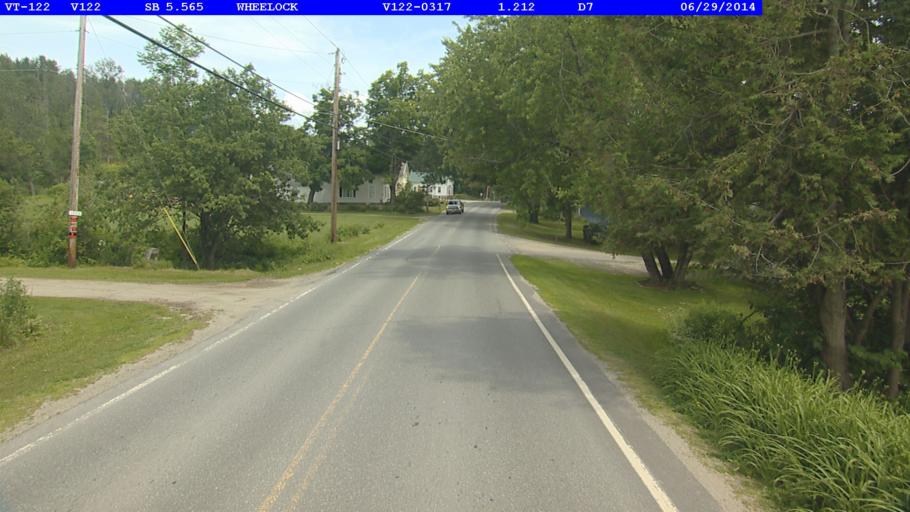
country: US
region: Vermont
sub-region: Caledonia County
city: Lyndonville
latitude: 44.5881
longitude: -72.0852
